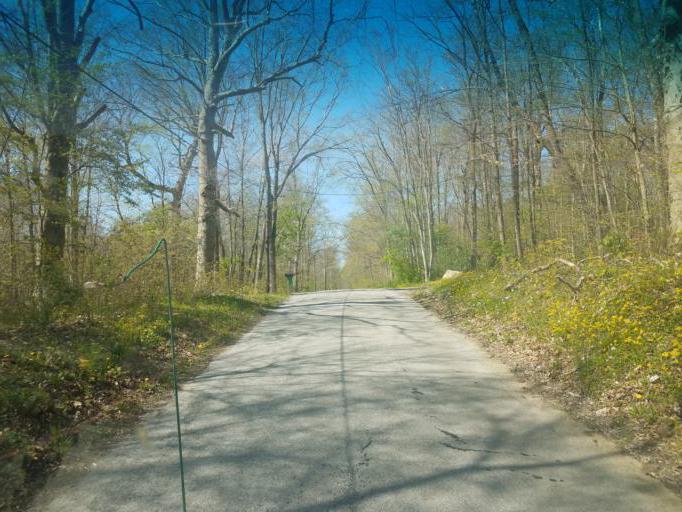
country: US
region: Ohio
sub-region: Medina County
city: Lodi
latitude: 40.9683
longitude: -82.0250
